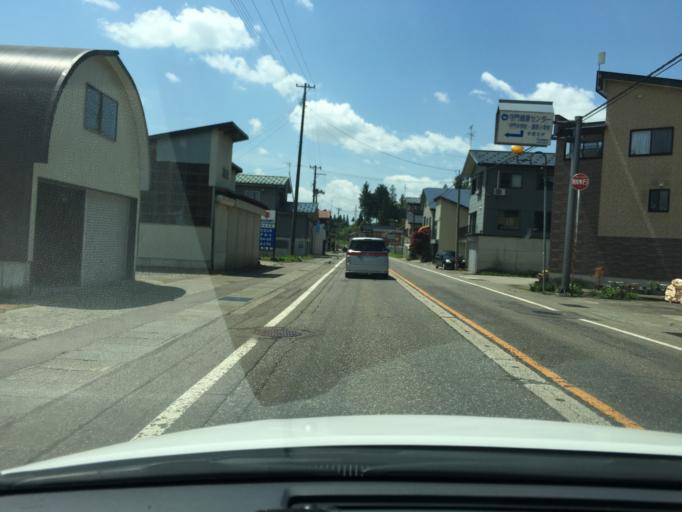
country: JP
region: Niigata
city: Tochio-honcho
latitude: 37.3181
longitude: 139.0155
